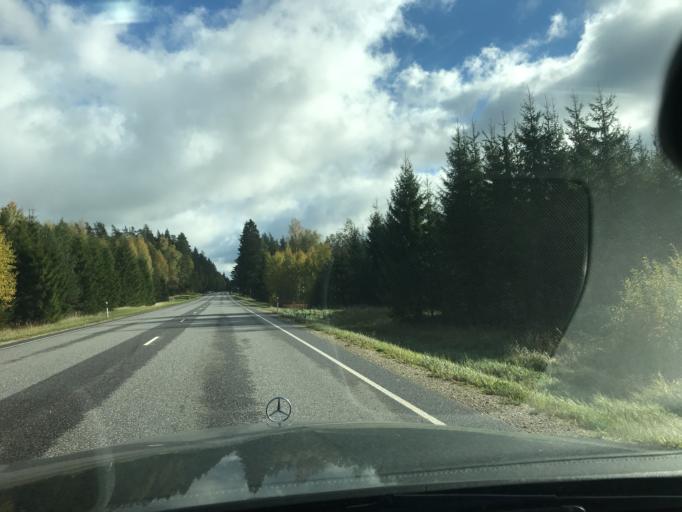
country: EE
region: Vorumaa
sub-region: Voru linn
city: Voru
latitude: 57.7668
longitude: 27.1769
